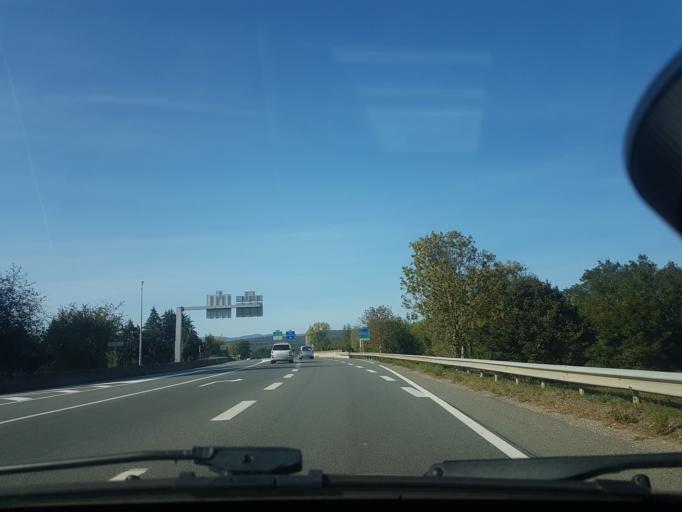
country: FR
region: Franche-Comte
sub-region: Territoire de Belfort
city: Chevremont
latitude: 47.6474
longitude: 6.9172
